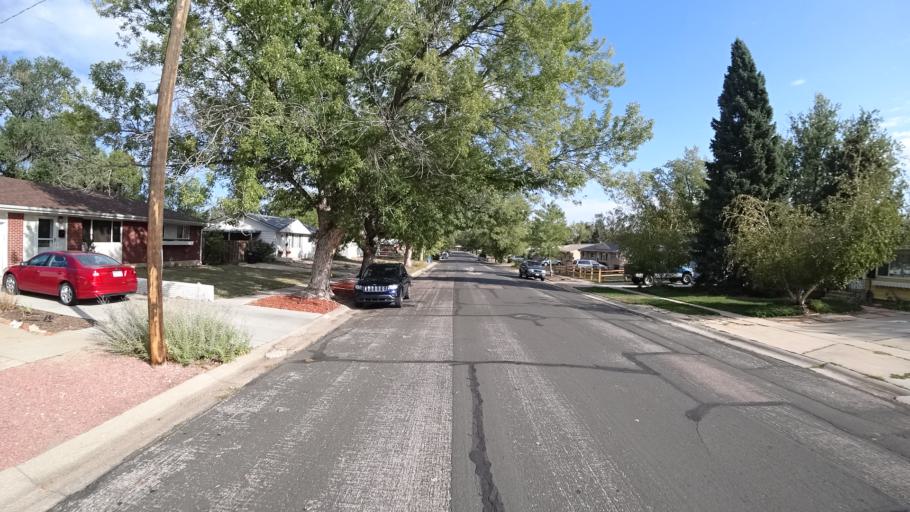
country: US
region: Colorado
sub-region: El Paso County
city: Colorado Springs
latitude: 38.8563
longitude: -104.7633
